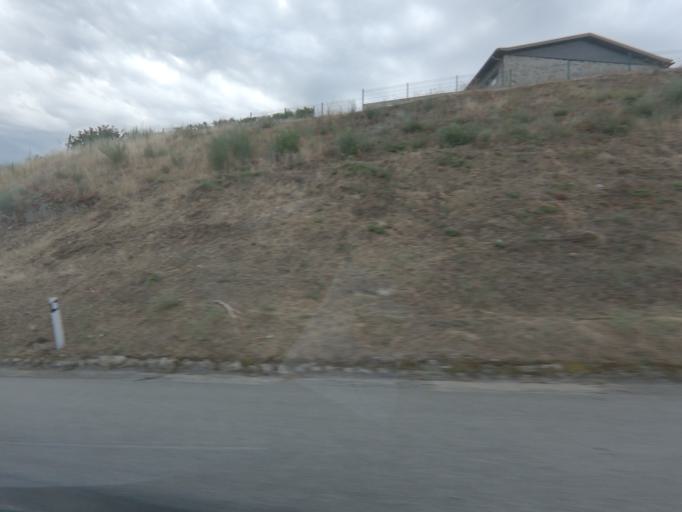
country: PT
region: Viseu
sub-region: Lamego
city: Lamego
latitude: 41.0755
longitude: -7.8089
